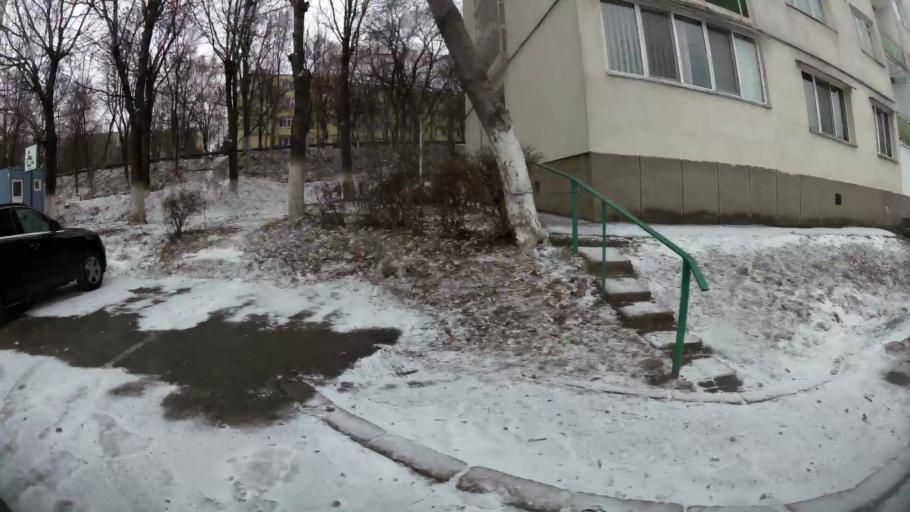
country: RO
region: Prahova
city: Ploiesti
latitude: 44.9550
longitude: 26.0105
